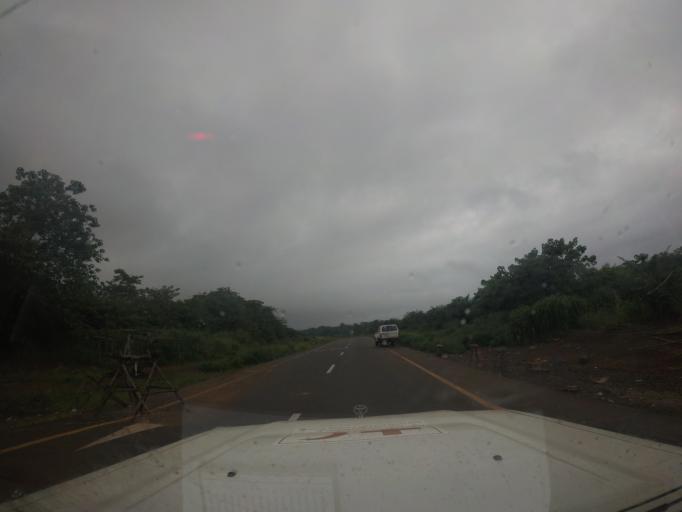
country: SL
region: Eastern Province
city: Hangha
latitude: 8.0178
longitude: -11.1099
